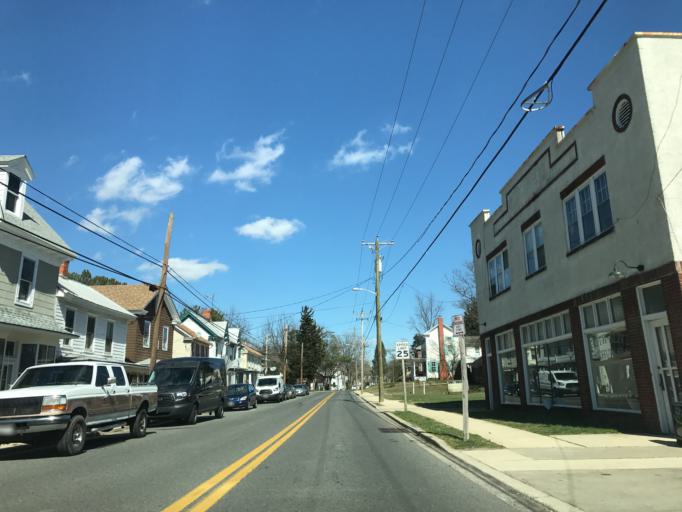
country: US
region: Maryland
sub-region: Queen Anne's County
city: Kingstown
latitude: 39.1424
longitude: -75.9851
